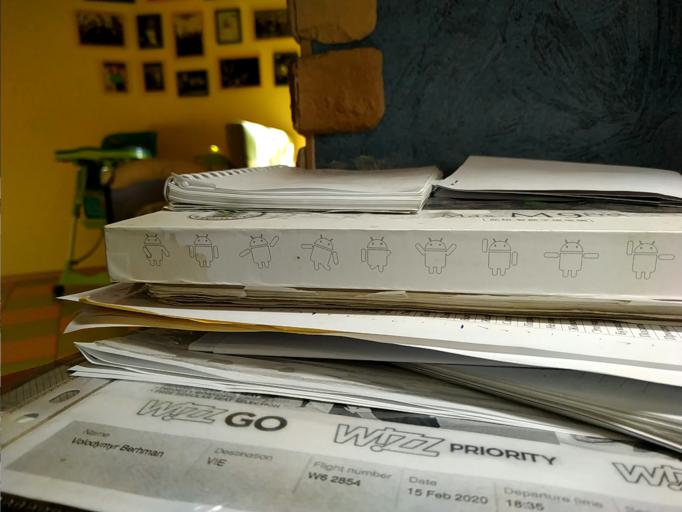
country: RU
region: Novgorod
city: Kholm
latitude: 57.3006
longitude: 31.2236
